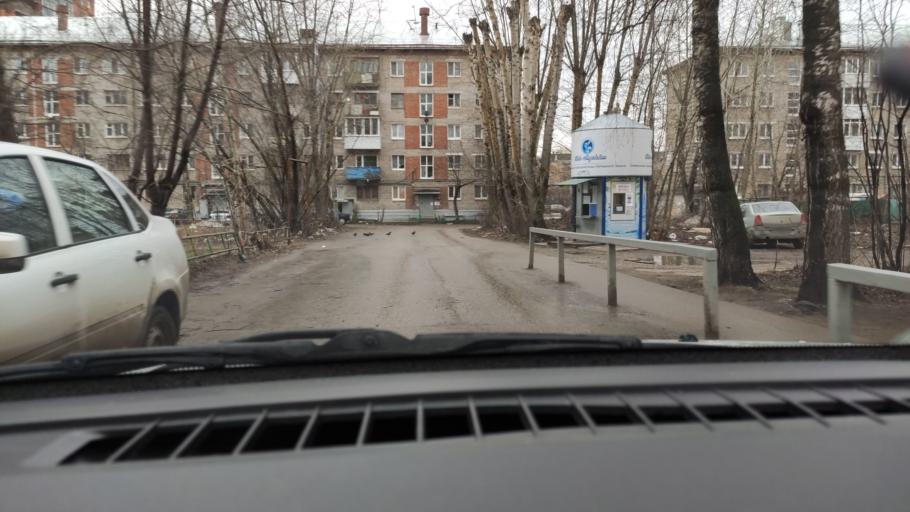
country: RU
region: Perm
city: Perm
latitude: 58.1104
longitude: 56.3068
